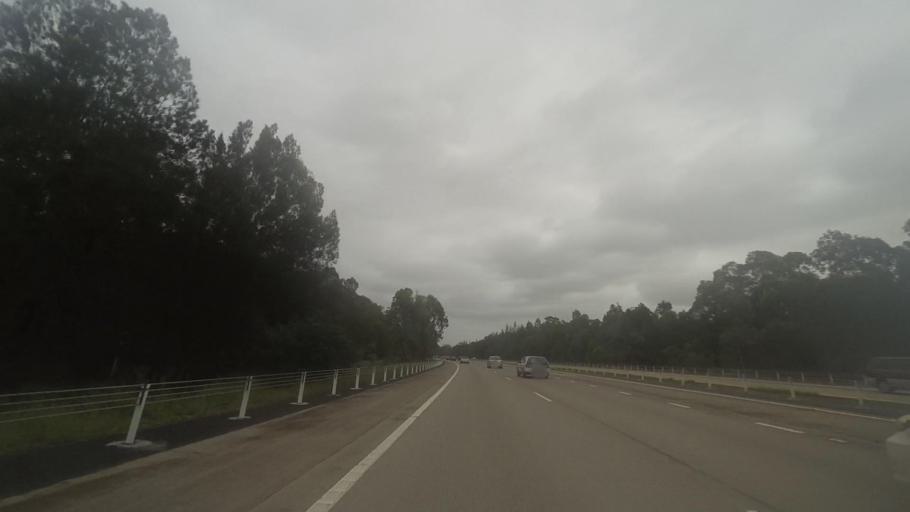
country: AU
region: New South Wales
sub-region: Port Stephens Shire
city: Raymond Terrace
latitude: -32.7042
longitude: 151.8004
